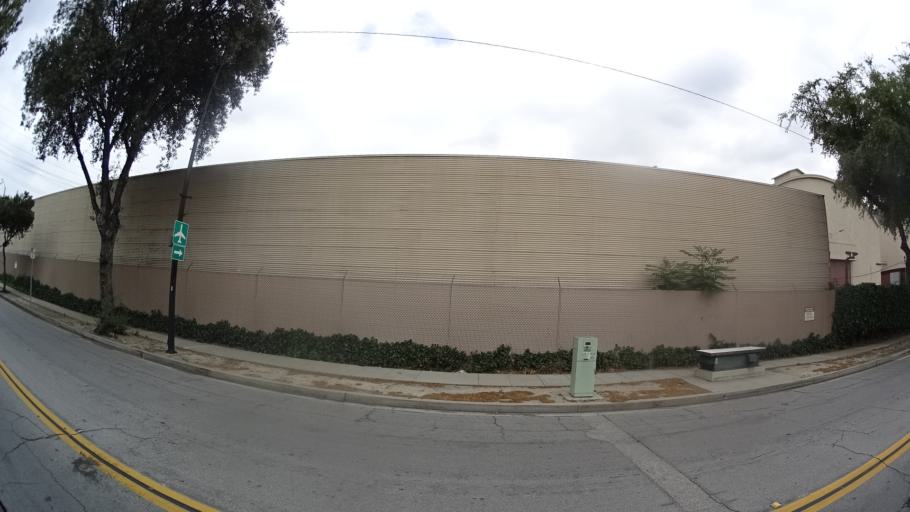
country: US
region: California
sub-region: Los Angeles County
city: Universal City
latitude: 34.1592
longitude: -118.3475
